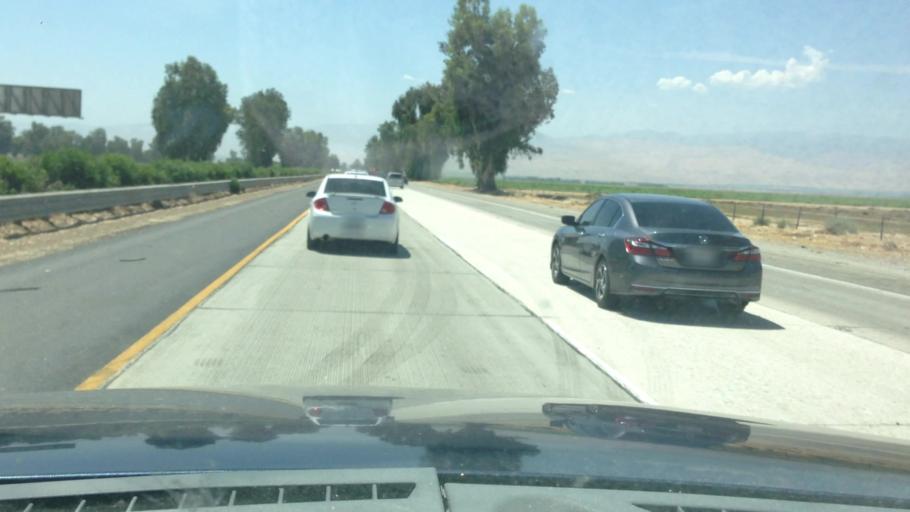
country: US
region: California
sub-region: Kern County
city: Greenfield
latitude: 35.1917
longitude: -119.0077
